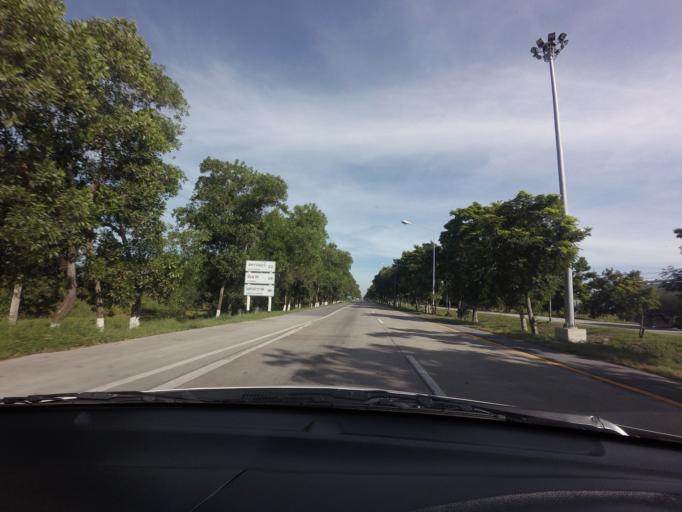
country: TH
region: Suphan Buri
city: Bang Pla Ma
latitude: 14.3308
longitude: 100.2096
